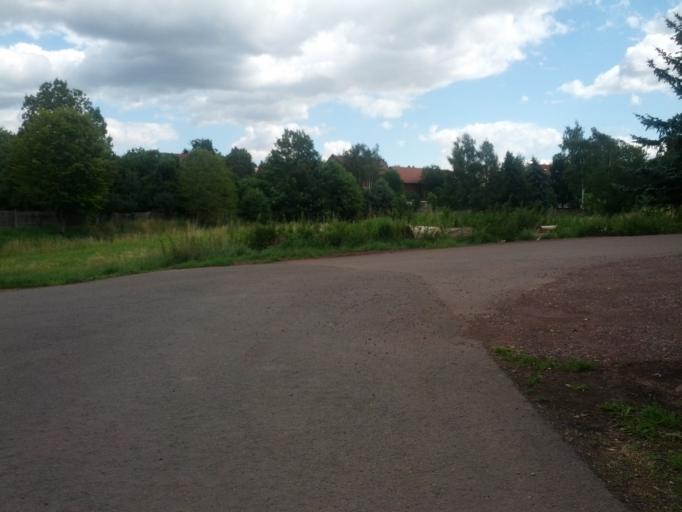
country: DE
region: Thuringia
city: Bischofroda
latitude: 50.9892
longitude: 10.3797
